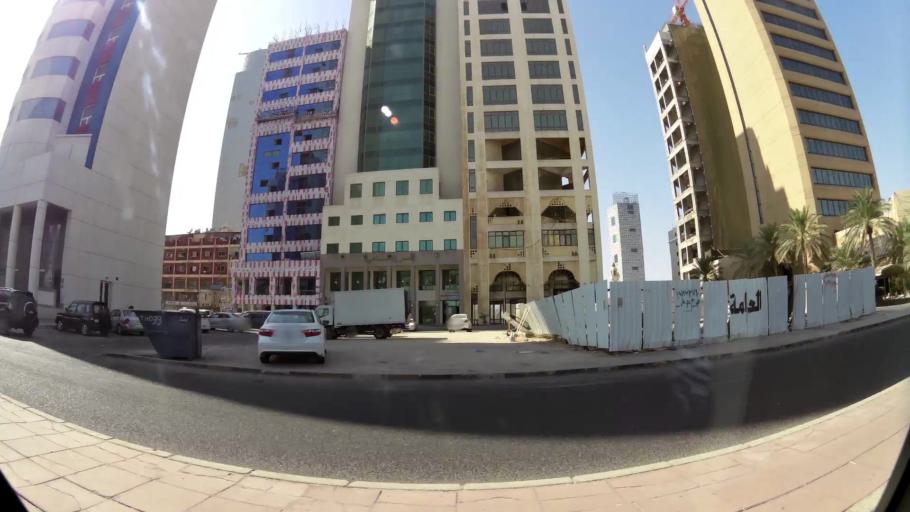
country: KW
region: Al Asimah
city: Kuwait City
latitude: 29.3844
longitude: 47.9886
